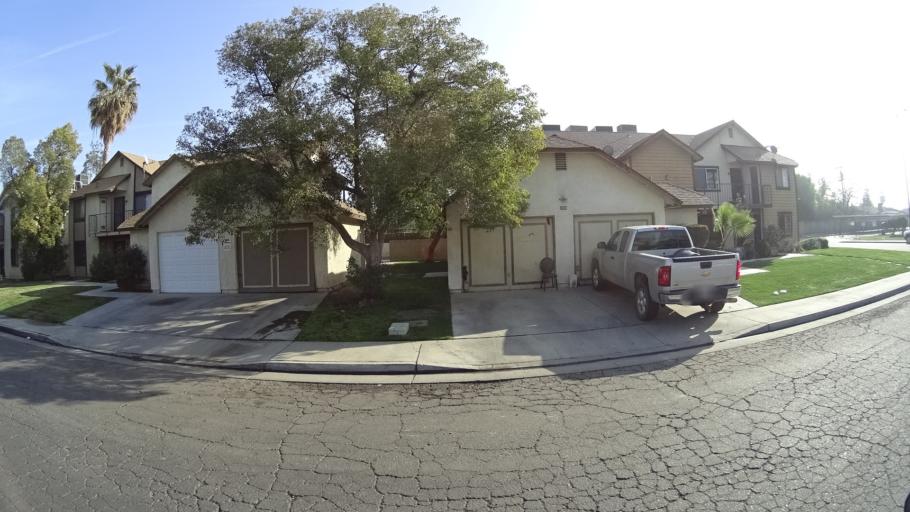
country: US
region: California
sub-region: Kern County
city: Bakersfield
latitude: 35.3290
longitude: -119.0361
